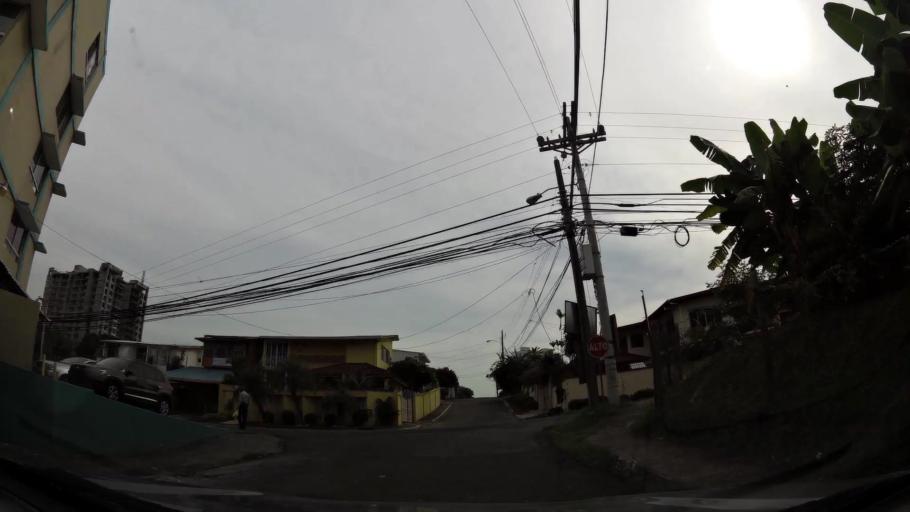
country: PA
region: Panama
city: Panama
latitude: 9.0132
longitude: -79.5184
